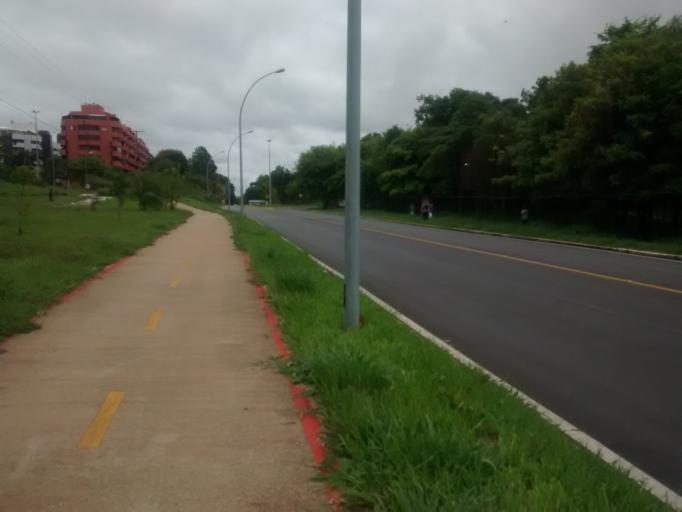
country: BR
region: Federal District
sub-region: Brasilia
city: Brasilia
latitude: -15.7429
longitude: -47.8867
